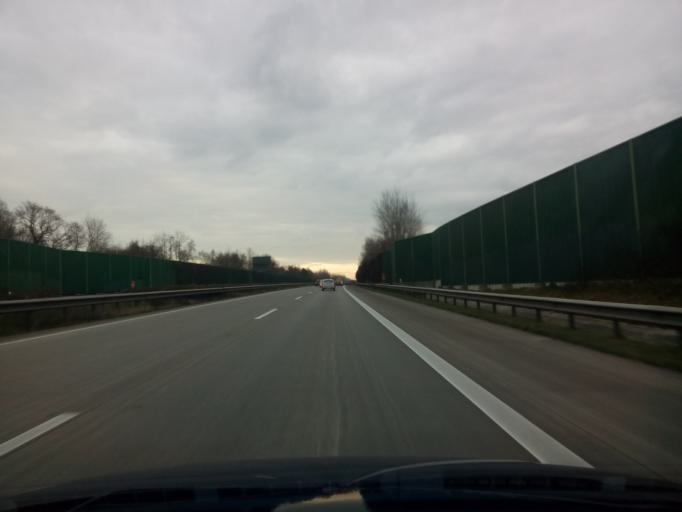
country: DE
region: Lower Saxony
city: Schiffdorf
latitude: 53.5137
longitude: 8.6283
